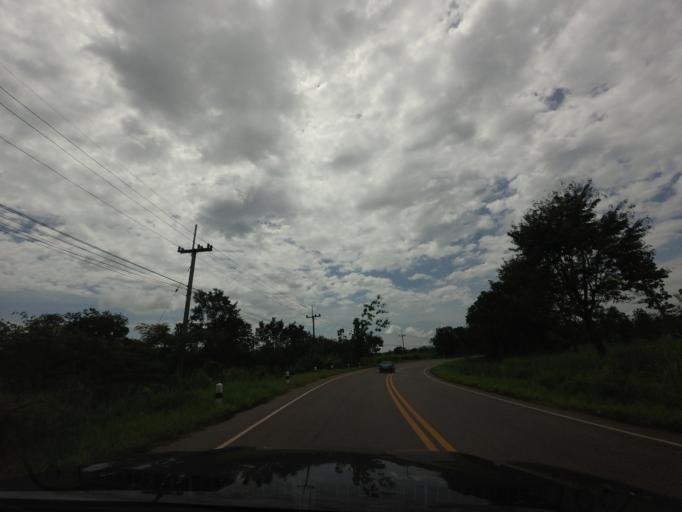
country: TH
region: Changwat Udon Thani
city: Nam Som
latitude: 17.8169
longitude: 102.2726
